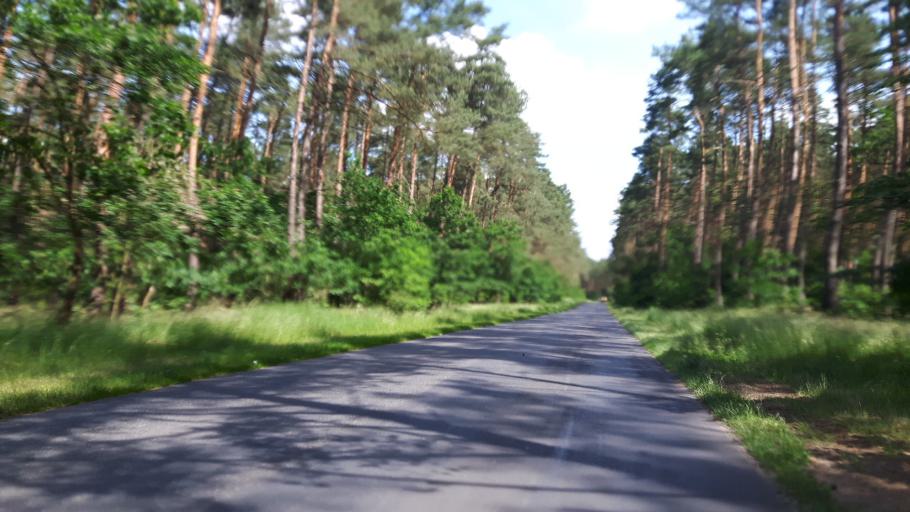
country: PL
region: West Pomeranian Voivodeship
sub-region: Powiat goleniowski
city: Goleniow
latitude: 53.5106
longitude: 14.7873
